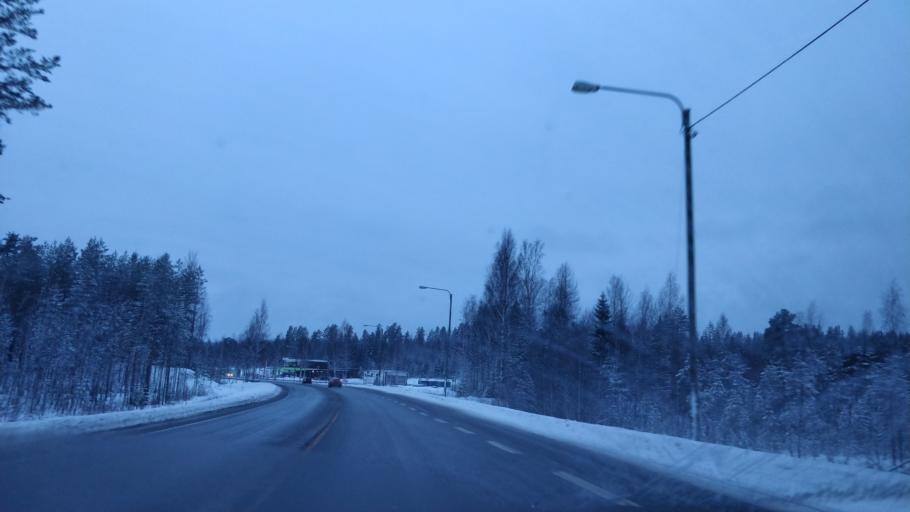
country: FI
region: Central Finland
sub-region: AEaenekoski
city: AEaenekoski
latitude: 62.8228
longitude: 25.8057
